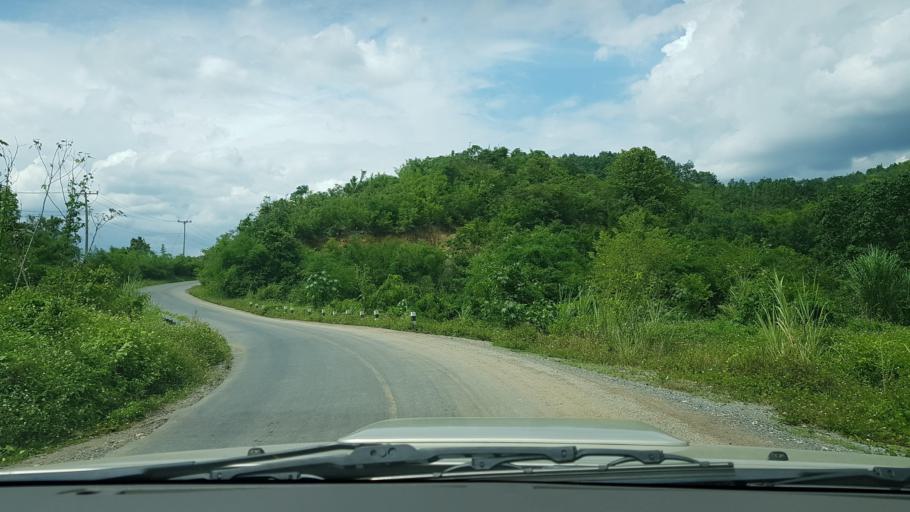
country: LA
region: Loungnamtha
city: Muang Nale
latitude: 20.2418
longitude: 101.5764
